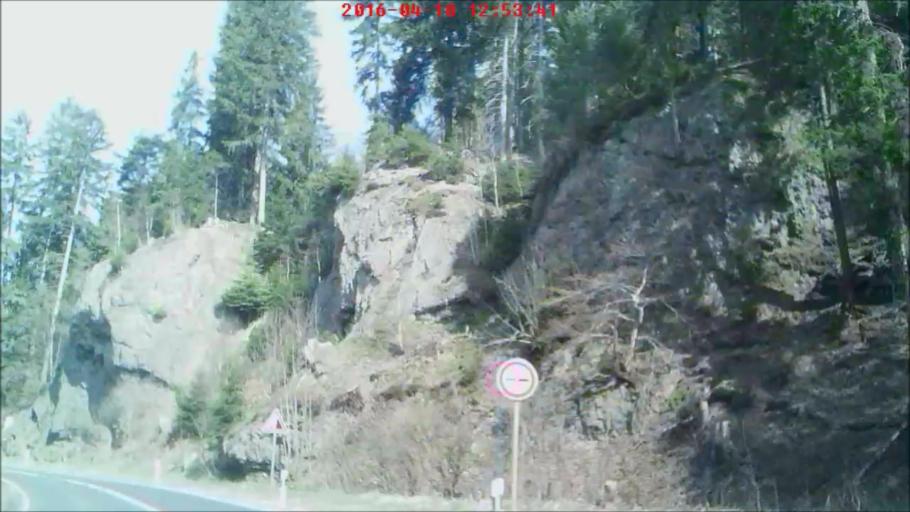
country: DE
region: Thuringia
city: Pappenheim
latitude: 50.8123
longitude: 10.5140
